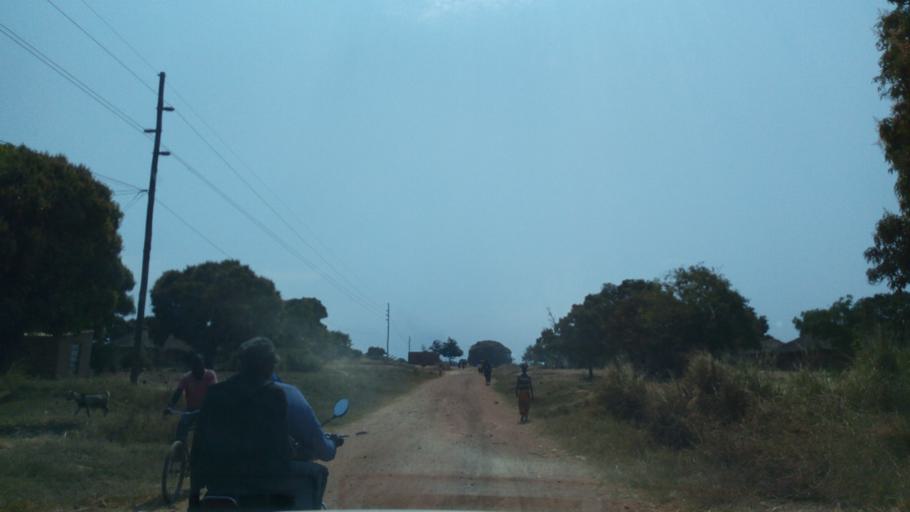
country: ZM
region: Northern
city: Kaputa
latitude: -8.4510
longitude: 28.9076
